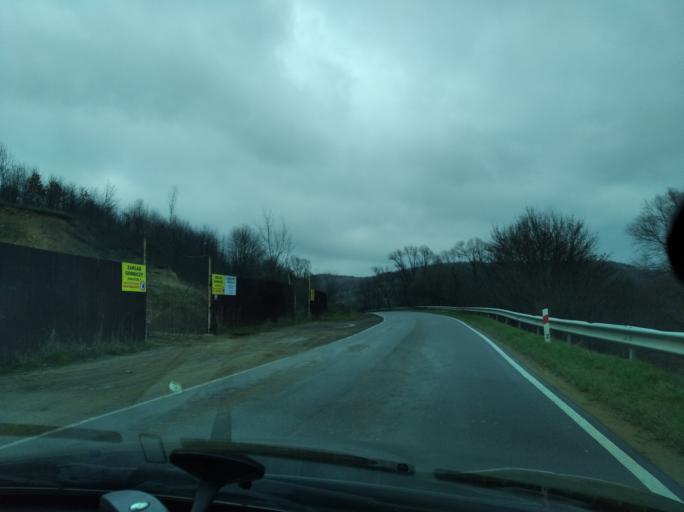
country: PL
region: Subcarpathian Voivodeship
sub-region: Powiat przeworski
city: Manasterz
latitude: 49.9221
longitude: 22.3301
